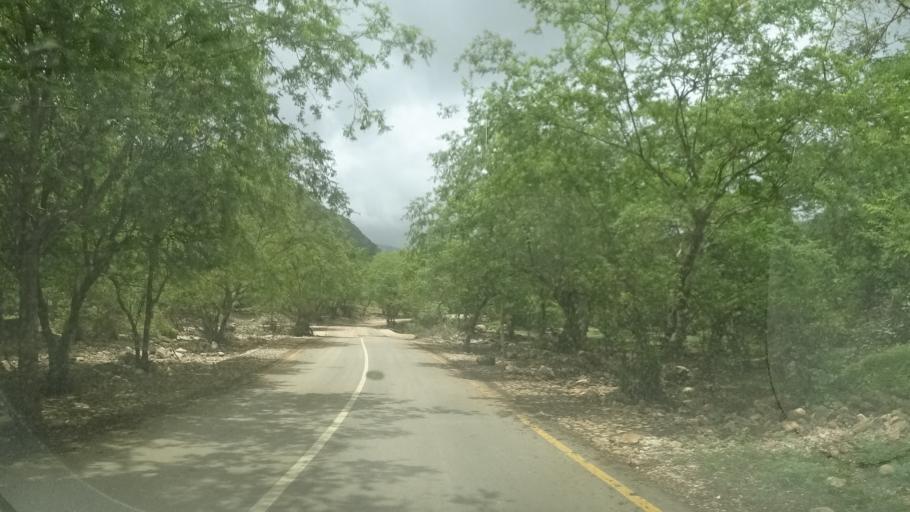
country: OM
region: Zufar
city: Salalah
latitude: 17.1044
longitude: 54.3516
